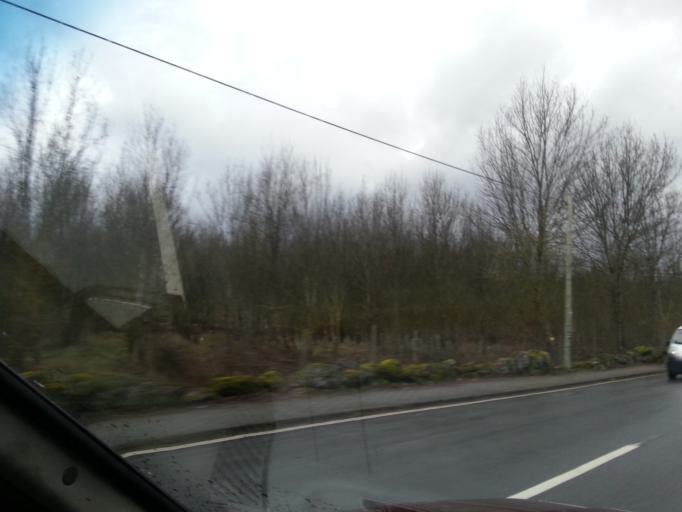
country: PT
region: Guarda
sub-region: Celorico da Beira
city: Celorico da Beira
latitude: 40.6260
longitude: -7.3317
